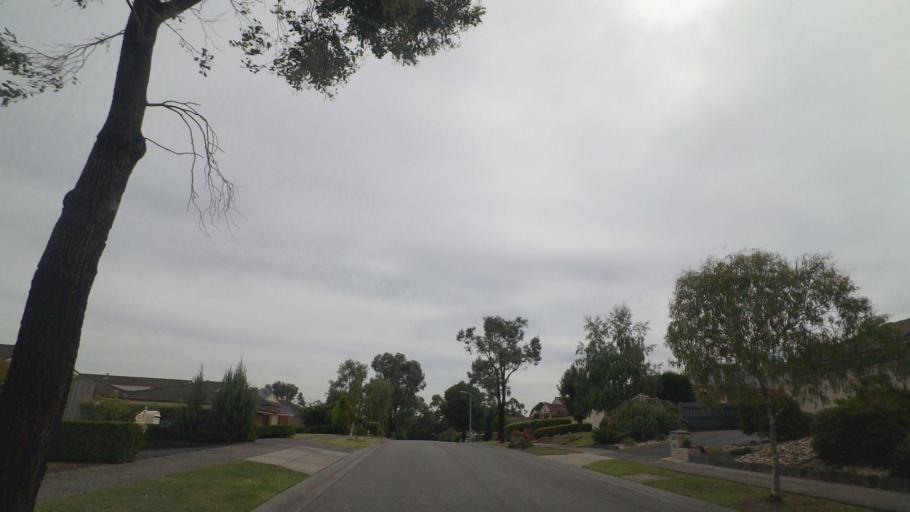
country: AU
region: Victoria
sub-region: Yarra Ranges
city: Kilsyth
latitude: -37.7815
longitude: 145.3384
